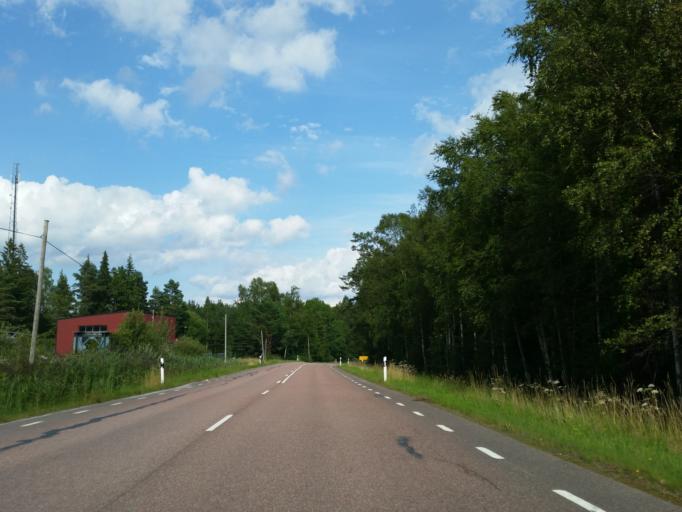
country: SE
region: Soedermanland
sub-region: Strangnas Kommun
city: Mariefred
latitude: 59.2215
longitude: 17.2578
